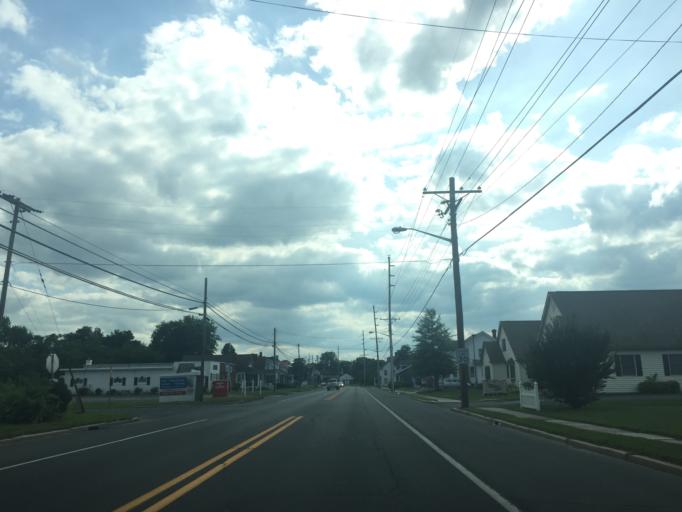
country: US
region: Delaware
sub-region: Sussex County
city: Georgetown
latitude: 38.6970
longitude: -75.3750
